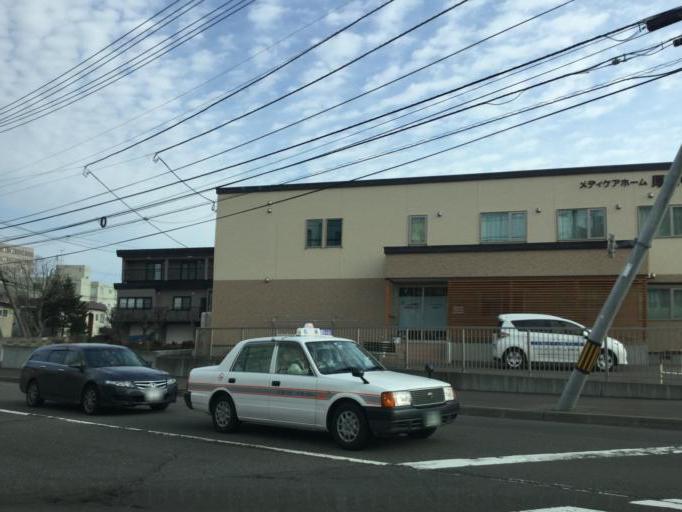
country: JP
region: Hokkaido
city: Sapporo
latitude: 43.0293
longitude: 141.4562
